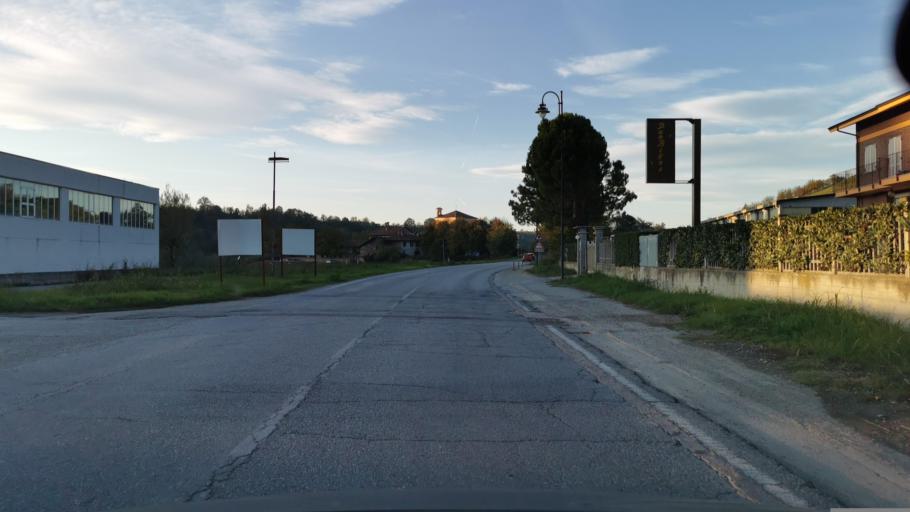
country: IT
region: Piedmont
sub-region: Provincia di Cuneo
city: Dogliani
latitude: 44.5414
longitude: 7.9290
